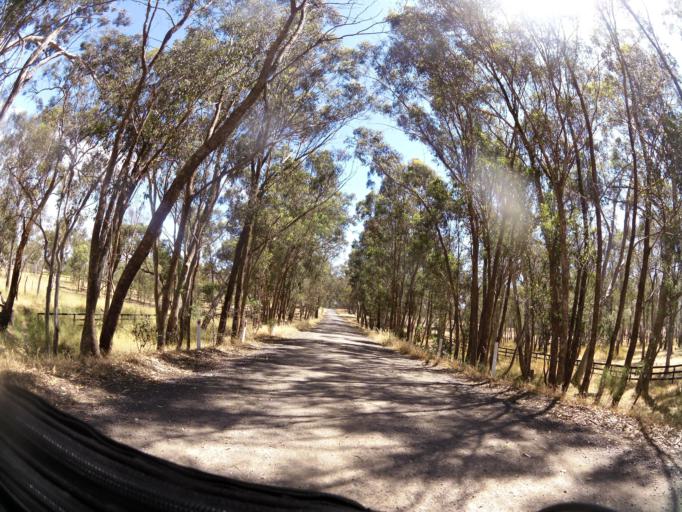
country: AU
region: Victoria
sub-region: Campaspe
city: Kyabram
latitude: -36.8297
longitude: 145.0767
